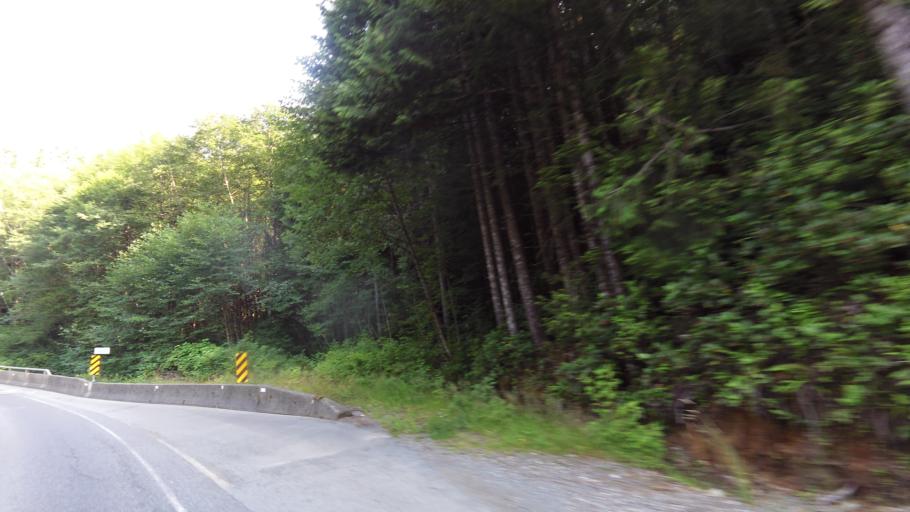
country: CA
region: British Columbia
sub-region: Regional District of Alberni-Clayoquot
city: Ucluelet
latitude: 49.0817
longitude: -125.4618
